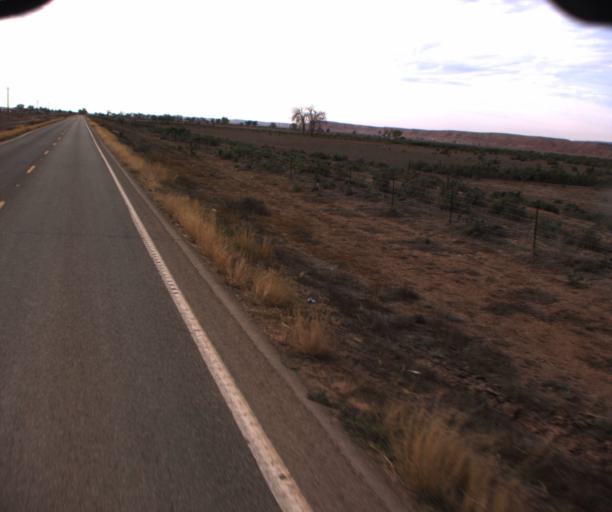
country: US
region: Arizona
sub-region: Apache County
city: Many Farms
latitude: 36.4315
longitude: -109.6068
